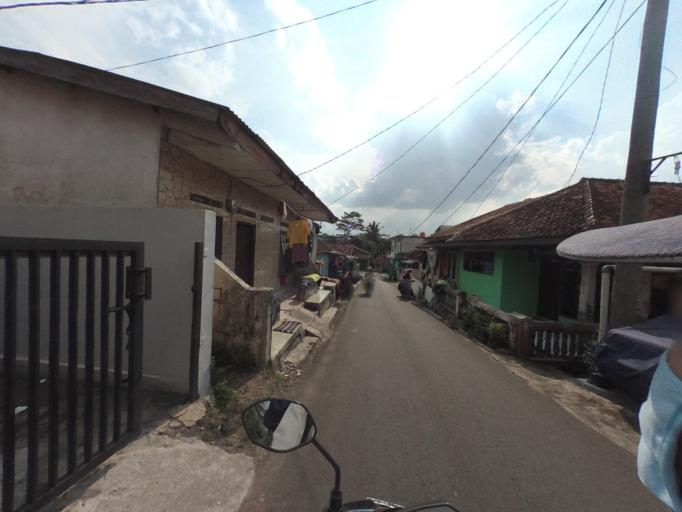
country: ID
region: West Java
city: Ciampea
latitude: -6.6066
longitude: 106.7084
